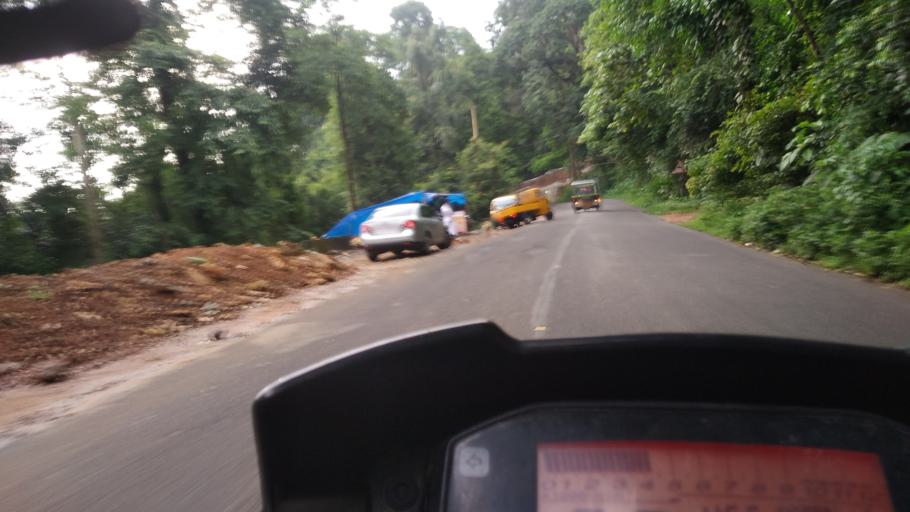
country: IN
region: Kerala
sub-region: Idukki
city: Kuttampuzha
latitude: 10.0654
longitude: 76.7717
